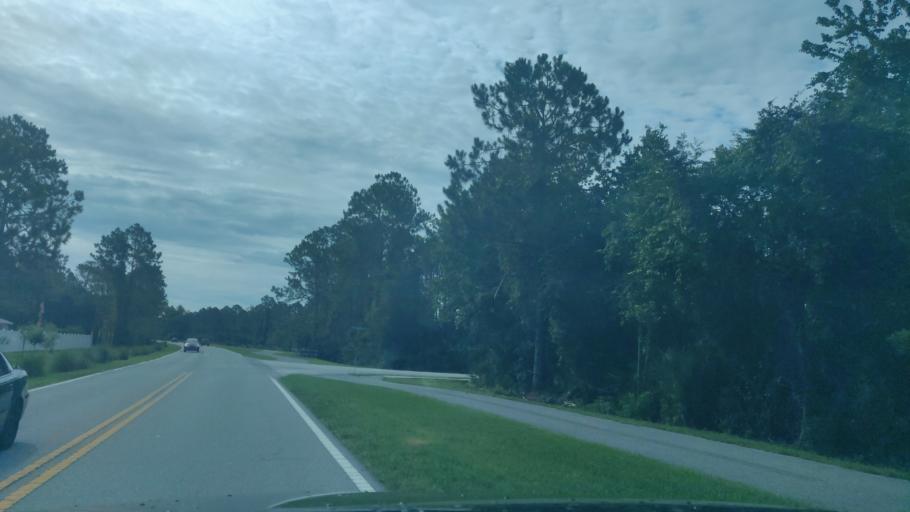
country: US
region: Florida
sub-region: Flagler County
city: Bunnell
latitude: 29.5180
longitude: -81.2373
